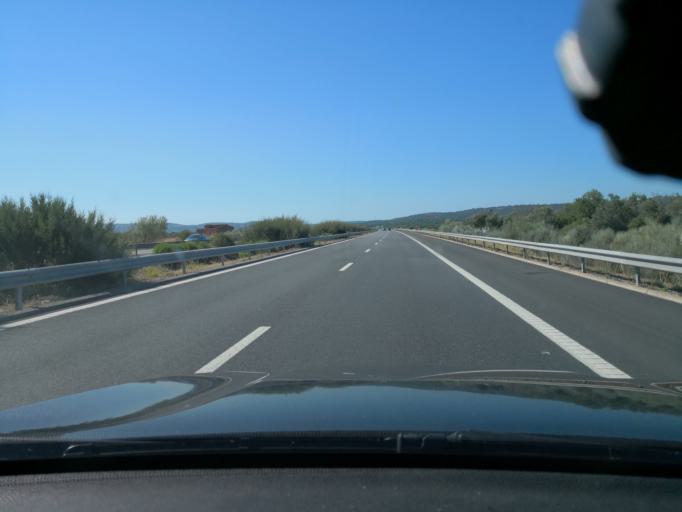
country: PT
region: Faro
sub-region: Silves
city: Sao Bartolomeu de Messines
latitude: 37.2194
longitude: -8.2426
